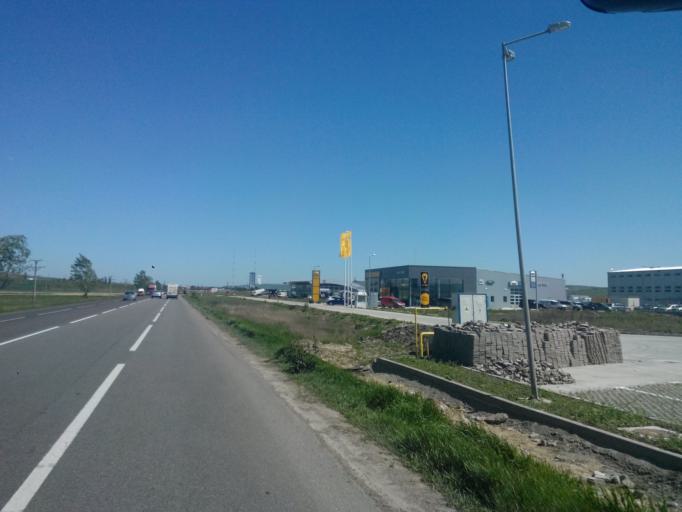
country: RO
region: Iasi
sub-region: Comuna Letcani
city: Letcani
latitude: 47.1896
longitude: 27.4323
